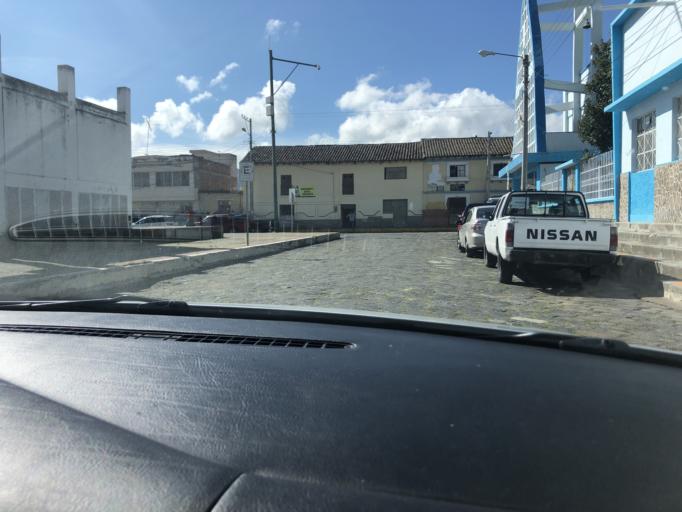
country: EC
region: Chimborazo
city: Riobamba
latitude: -1.7019
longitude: -78.7738
